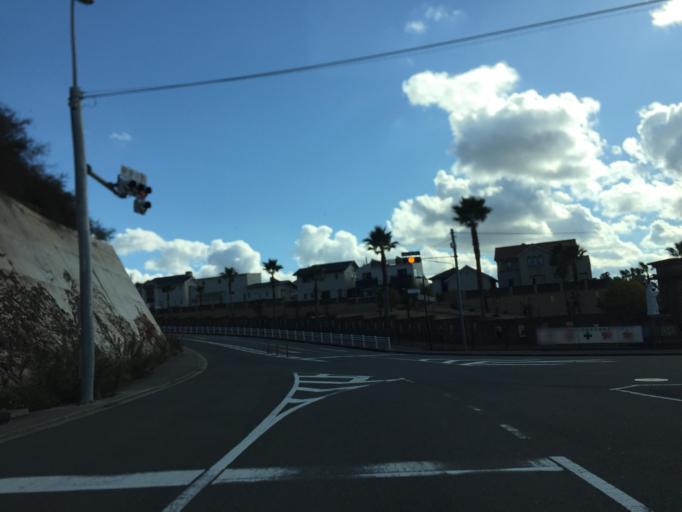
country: JP
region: Wakayama
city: Wakayama-shi
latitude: 34.2737
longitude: 135.1504
